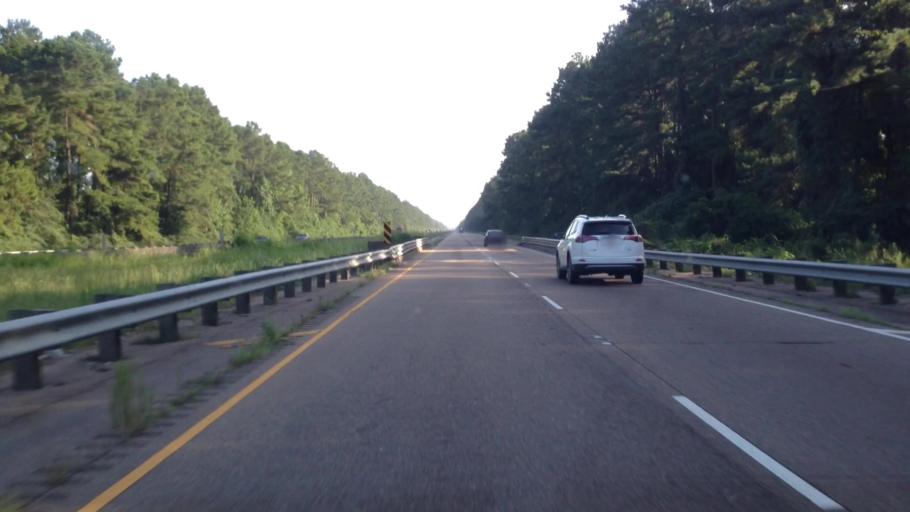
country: US
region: Louisiana
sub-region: Tangipahoa Parish
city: Independence
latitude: 30.6735
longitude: -90.5326
